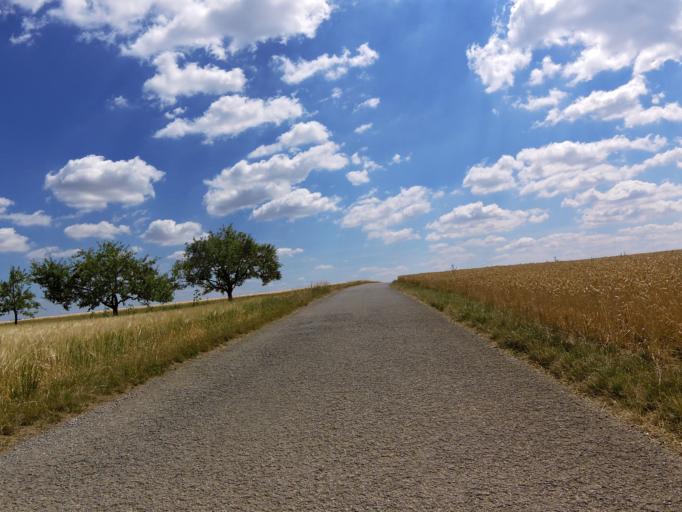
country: DE
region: Bavaria
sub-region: Regierungsbezirk Unterfranken
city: Hochberg
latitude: 49.7788
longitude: 9.8867
